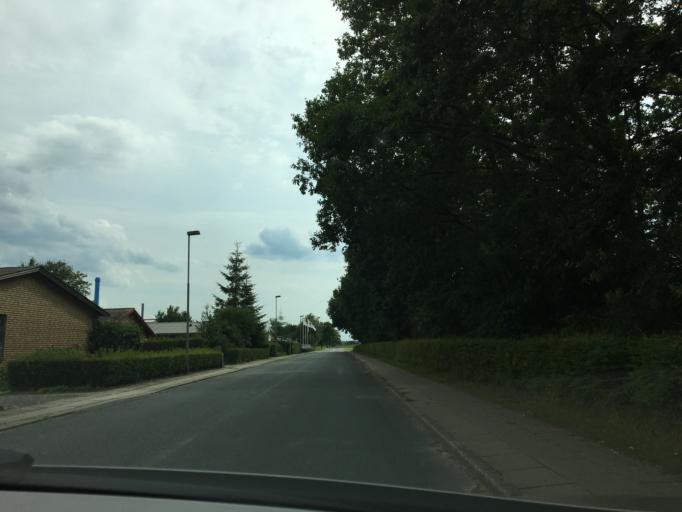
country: DK
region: Central Jutland
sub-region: Viborg Kommune
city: Stoholm
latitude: 56.4797
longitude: 9.1494
